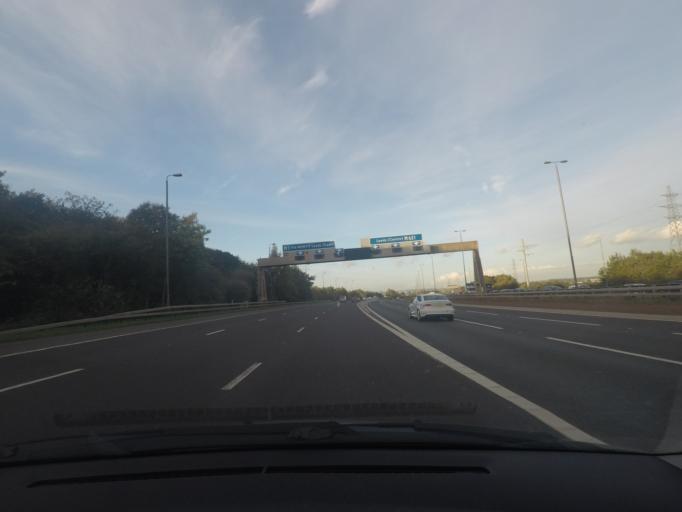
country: GB
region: England
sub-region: City and Borough of Leeds
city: Lofthouse
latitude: 53.7498
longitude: -1.5174
